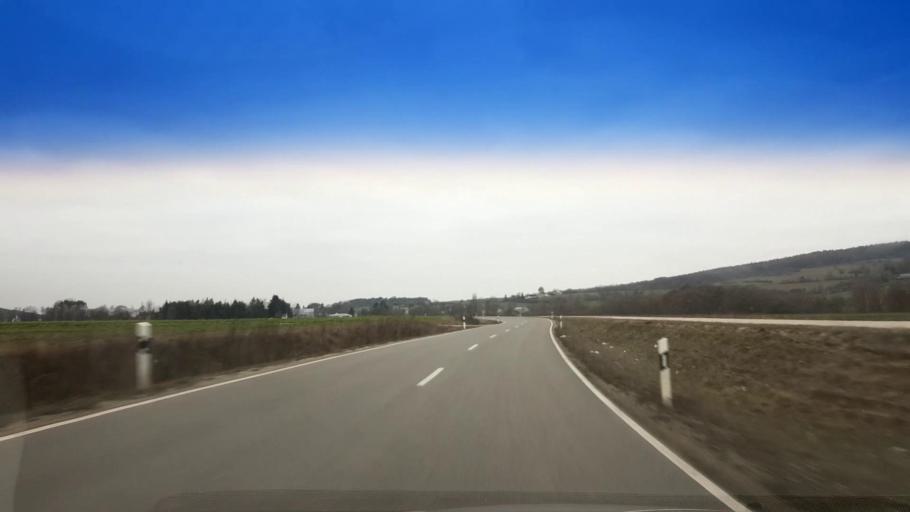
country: DE
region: Bavaria
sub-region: Upper Franconia
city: Pettstadt
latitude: 49.8032
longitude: 10.9401
